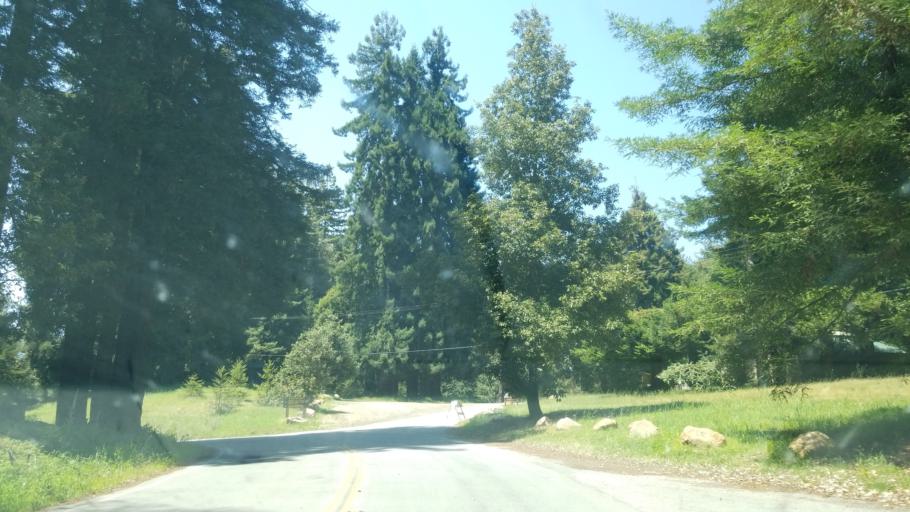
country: US
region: California
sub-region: Santa Cruz County
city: Interlaken
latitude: 37.0126
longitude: -121.7098
